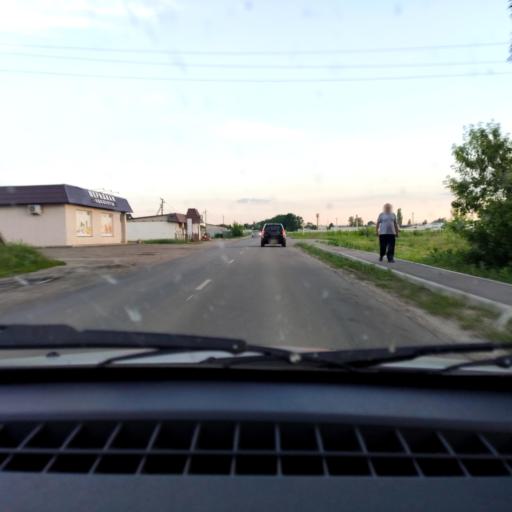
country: RU
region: Voronezj
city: Ramon'
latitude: 51.9354
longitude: 39.3478
